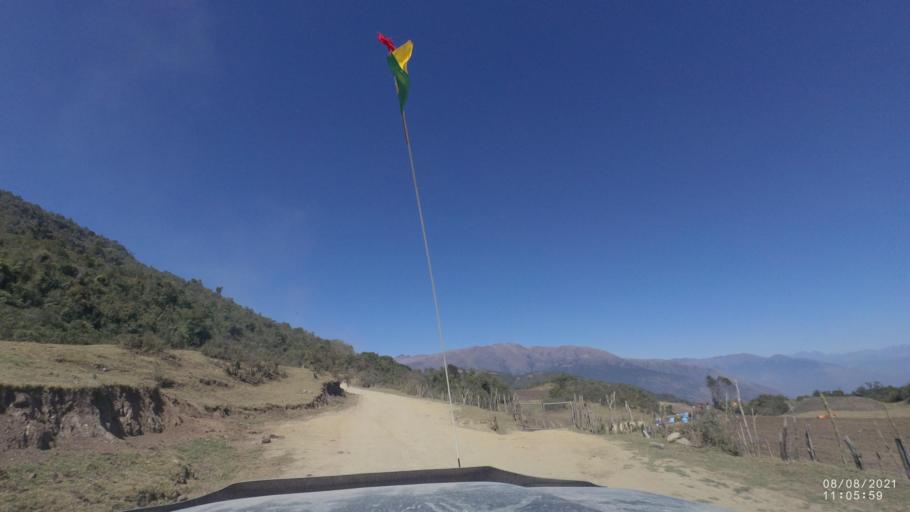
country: BO
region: Cochabamba
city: Colchani
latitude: -16.7602
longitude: -66.6839
